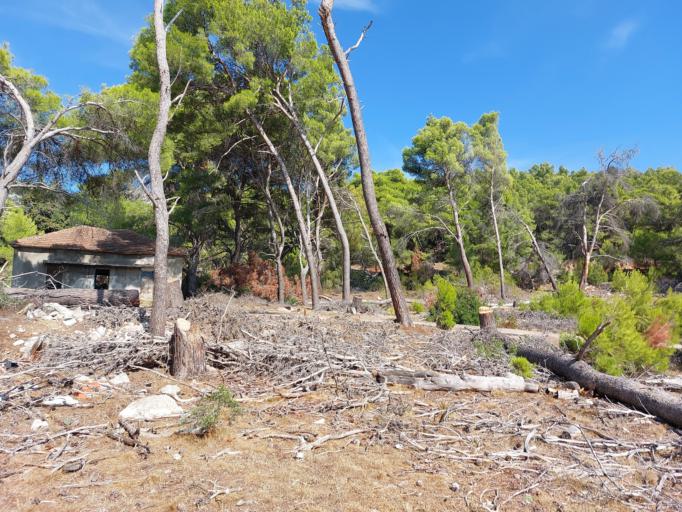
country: HR
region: Dubrovacko-Neretvanska
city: Smokvica
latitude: 42.7379
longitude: 16.8280
